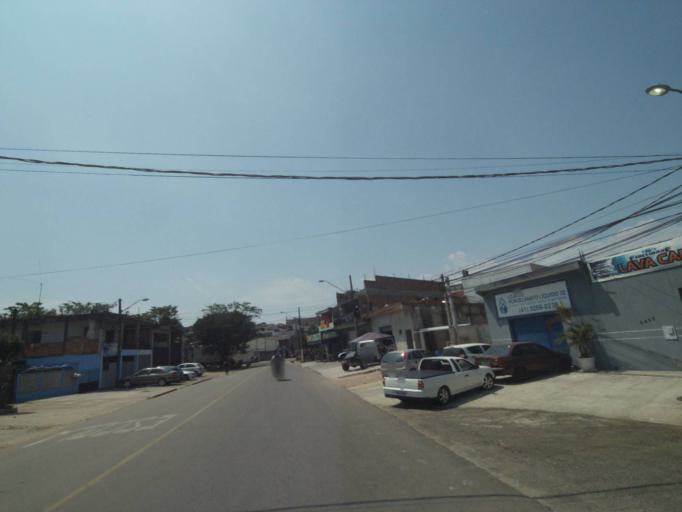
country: BR
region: Parana
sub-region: Curitiba
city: Curitiba
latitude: -25.4836
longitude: -49.3135
